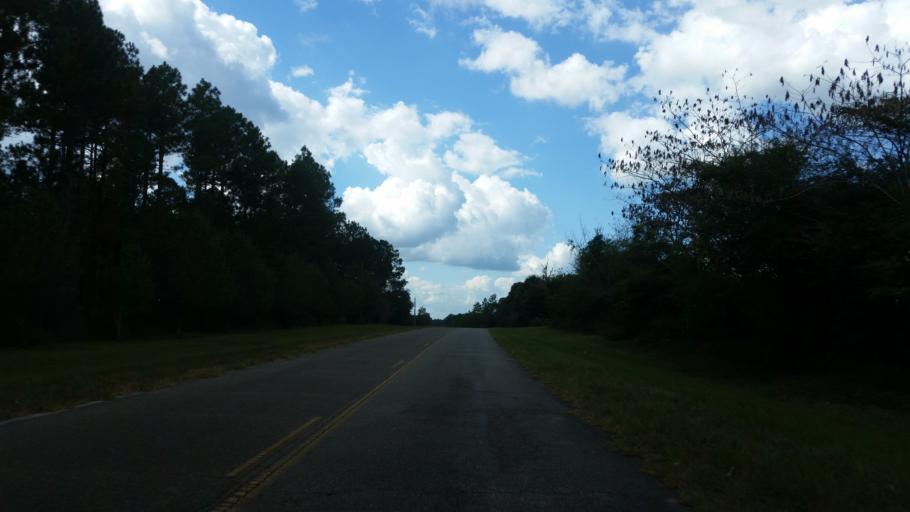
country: US
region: Alabama
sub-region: Escambia County
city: Atmore
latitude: 30.8974
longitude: -87.5596
